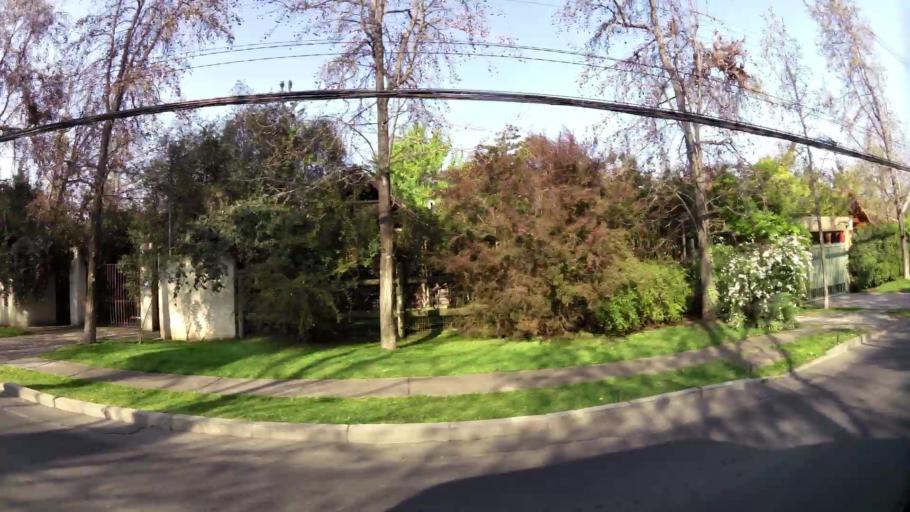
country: CL
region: Santiago Metropolitan
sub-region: Provincia de Santiago
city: Villa Presidente Frei, Nunoa, Santiago, Chile
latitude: -33.3620
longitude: -70.5298
